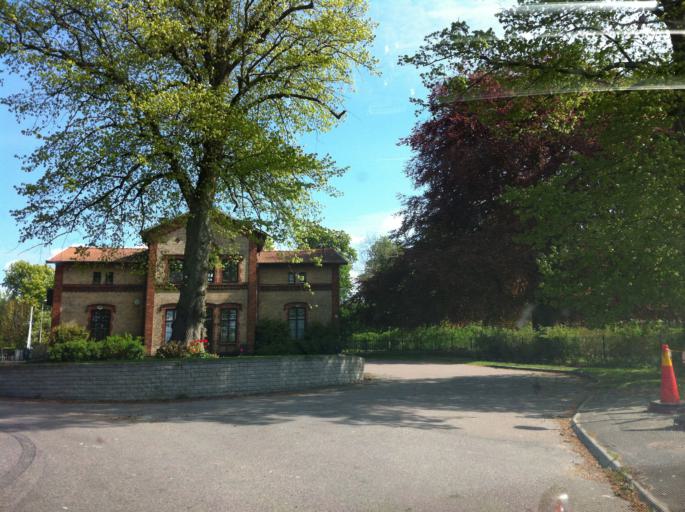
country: SE
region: Skane
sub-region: Landskrona
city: Asmundtorp
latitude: 55.8835
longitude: 12.9946
